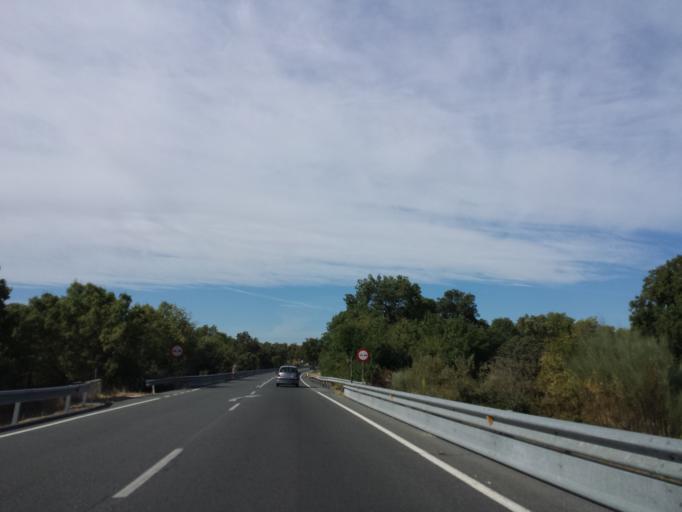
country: ES
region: Castille and Leon
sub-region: Provincia de Avila
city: Casavieja
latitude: 40.2771
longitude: -4.7394
